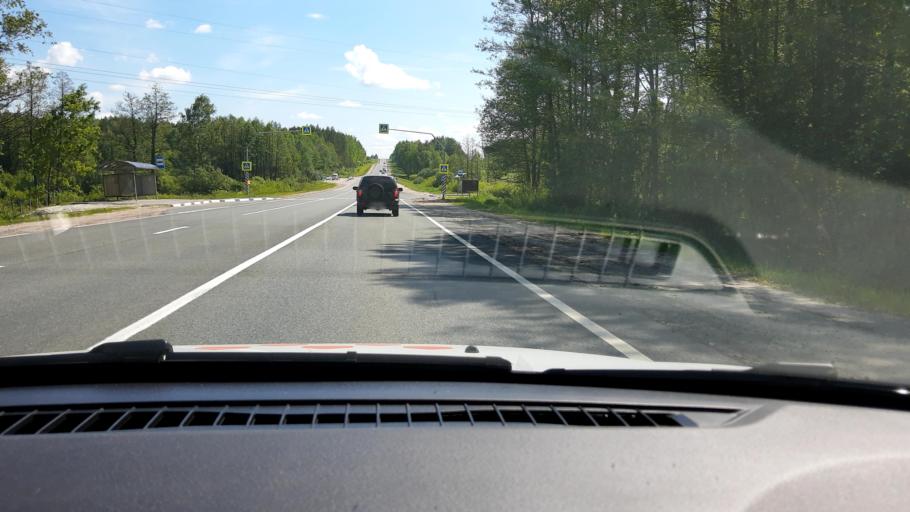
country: RU
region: Nizjnij Novgorod
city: Dal'neye Konstantinovo
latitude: 55.9827
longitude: 43.9710
